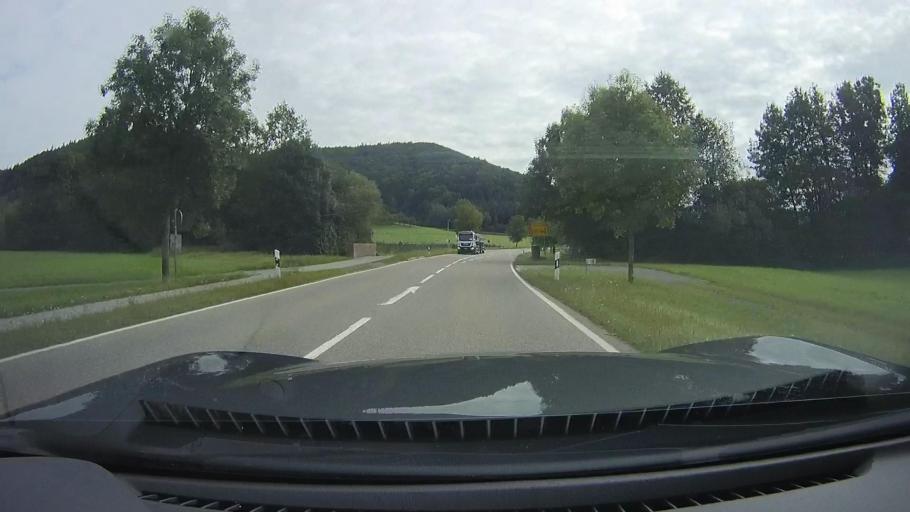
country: DE
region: Baden-Wuerttemberg
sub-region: Regierungsbezirk Stuttgart
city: Spiegelberg
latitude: 49.0172
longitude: 9.4689
